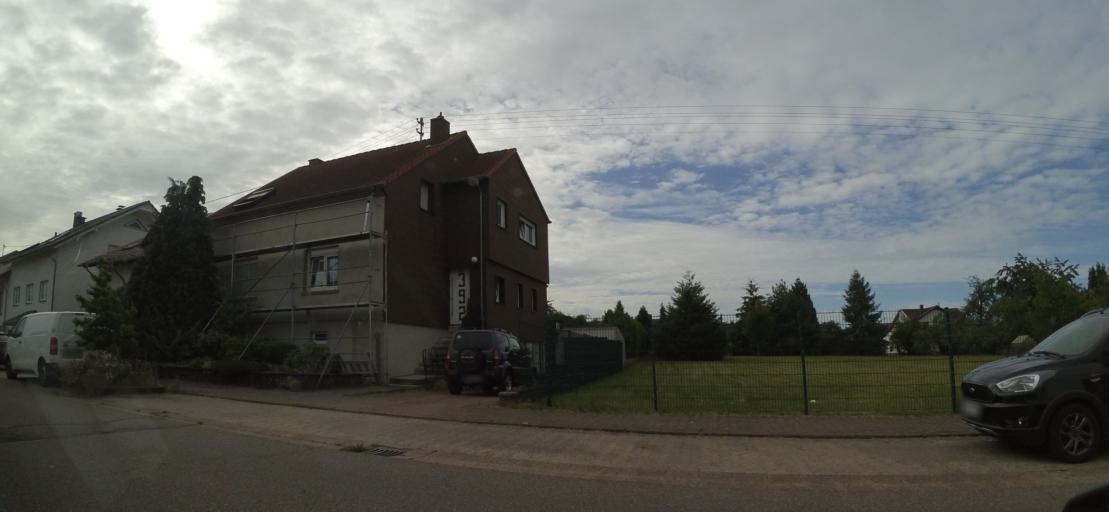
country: DE
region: Saarland
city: Schwalbach
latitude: 49.3089
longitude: 6.8312
